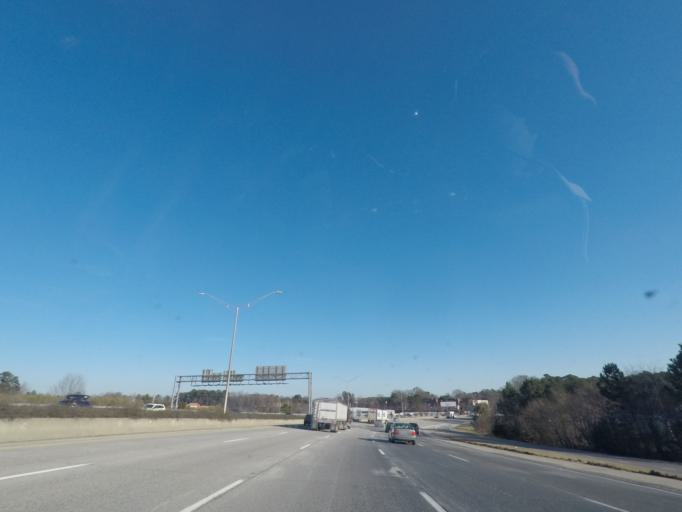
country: US
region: North Carolina
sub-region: Durham County
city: Durham
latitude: 36.0284
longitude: -78.9225
